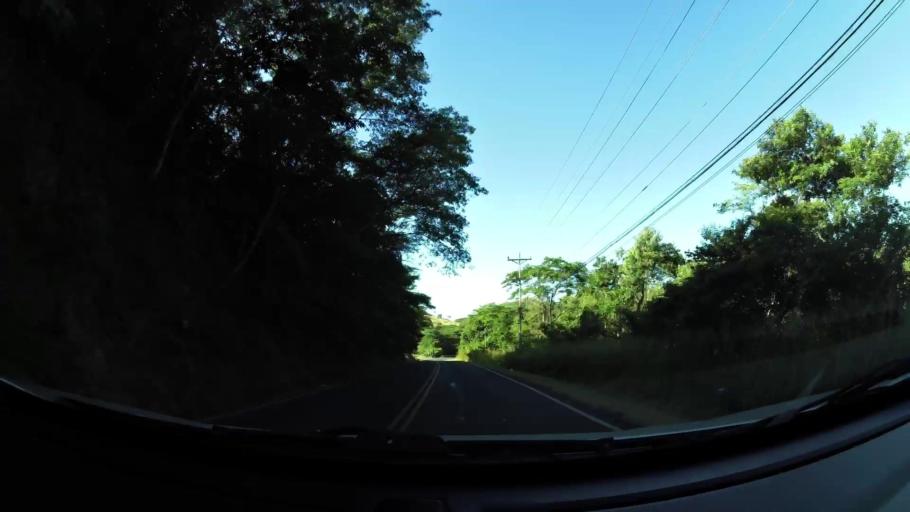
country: CR
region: Guanacaste
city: Belen
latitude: 10.3744
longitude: -85.6253
